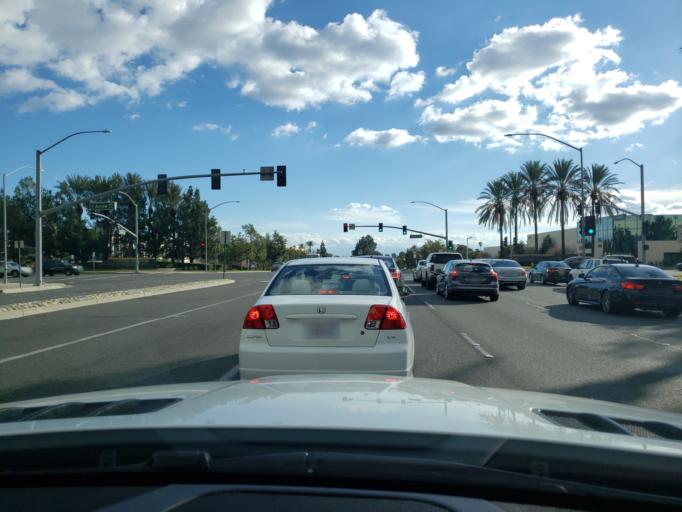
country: US
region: California
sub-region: San Bernardino County
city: Rancho Cucamonga
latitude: 34.0996
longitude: -117.5558
